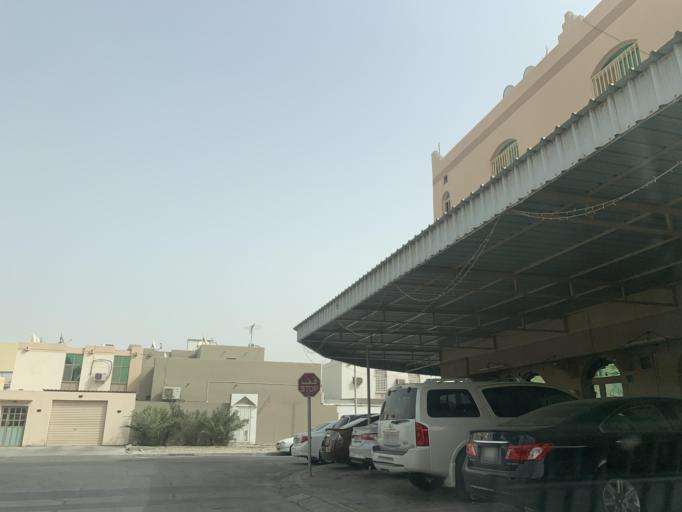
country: BH
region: Northern
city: Madinat `Isa
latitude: 26.1639
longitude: 50.5706
